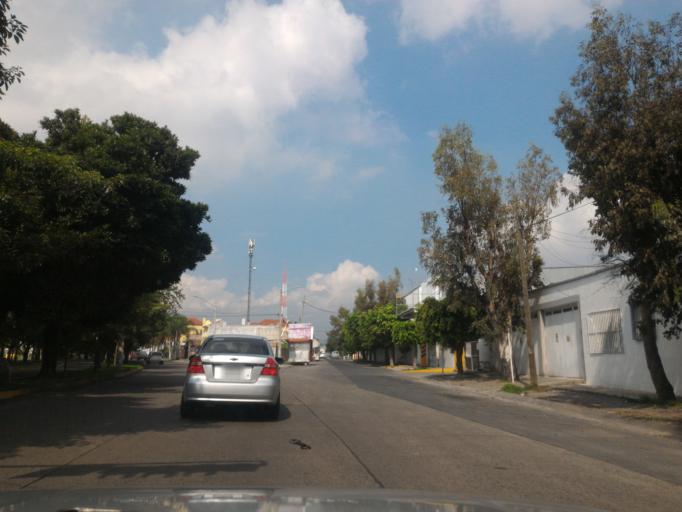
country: MX
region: Jalisco
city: Guadalajara
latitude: 20.6286
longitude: -103.3936
